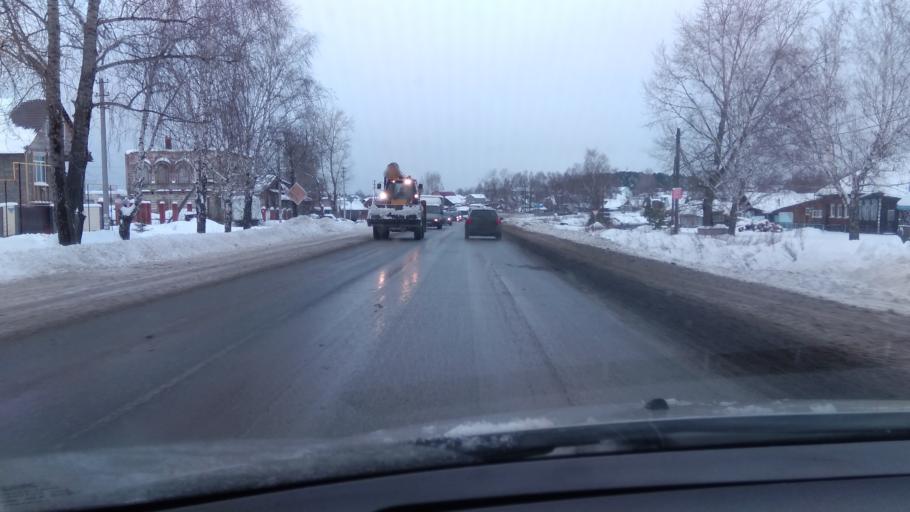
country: RU
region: Sverdlovsk
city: Nikolo-Pavlovskoye
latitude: 57.7840
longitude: 60.0582
